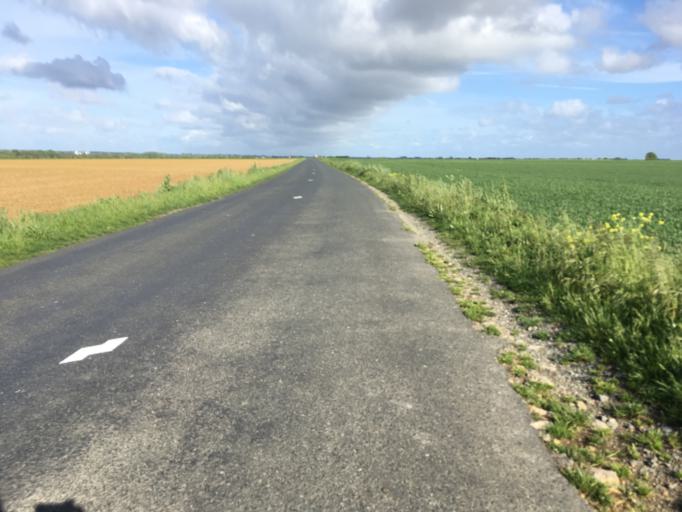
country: FR
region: Poitou-Charentes
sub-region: Departement de la Charente-Maritime
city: Verines
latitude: 46.1710
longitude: -0.8996
